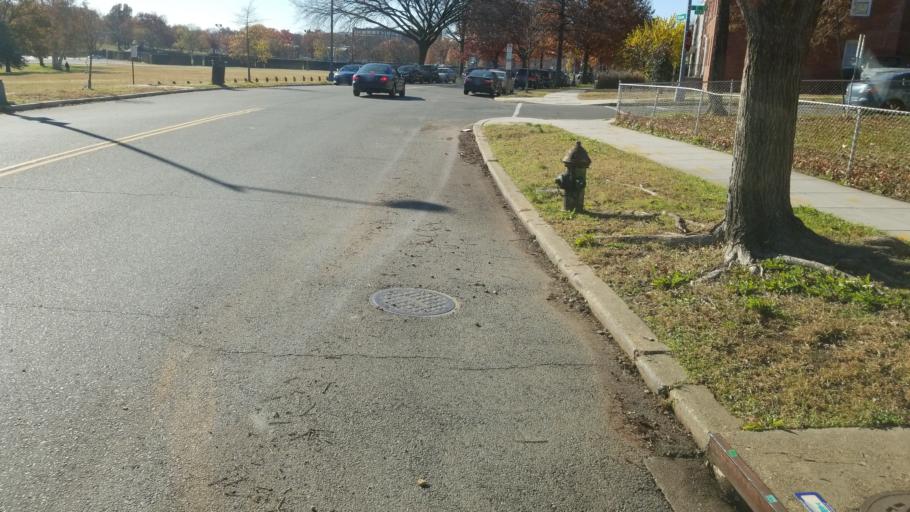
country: US
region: Maryland
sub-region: Prince George's County
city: Colmar Manor
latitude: 38.8959
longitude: -76.9712
